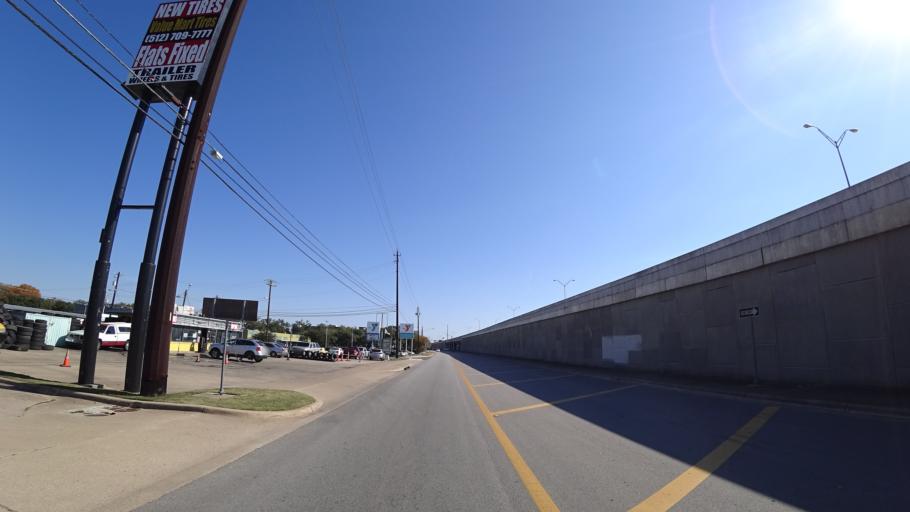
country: US
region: Texas
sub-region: Travis County
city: Barton Creek
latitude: 30.2356
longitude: -97.8547
